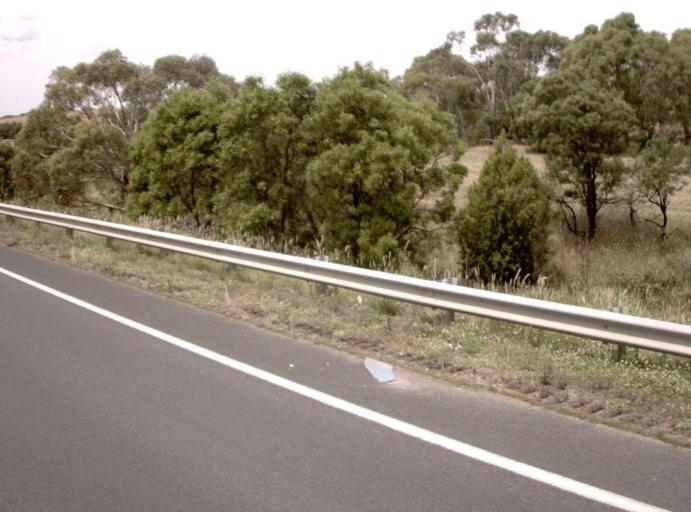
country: AU
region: Victoria
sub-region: Mornington Peninsula
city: Mount Martha
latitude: -38.2804
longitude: 145.0549
